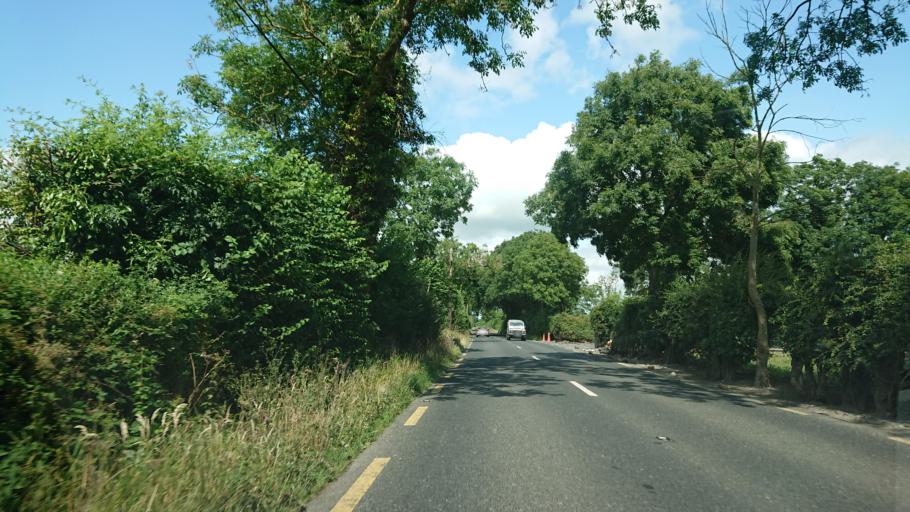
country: IE
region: Leinster
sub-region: Kildare
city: Kilcock
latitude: 53.3585
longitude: -6.6959
